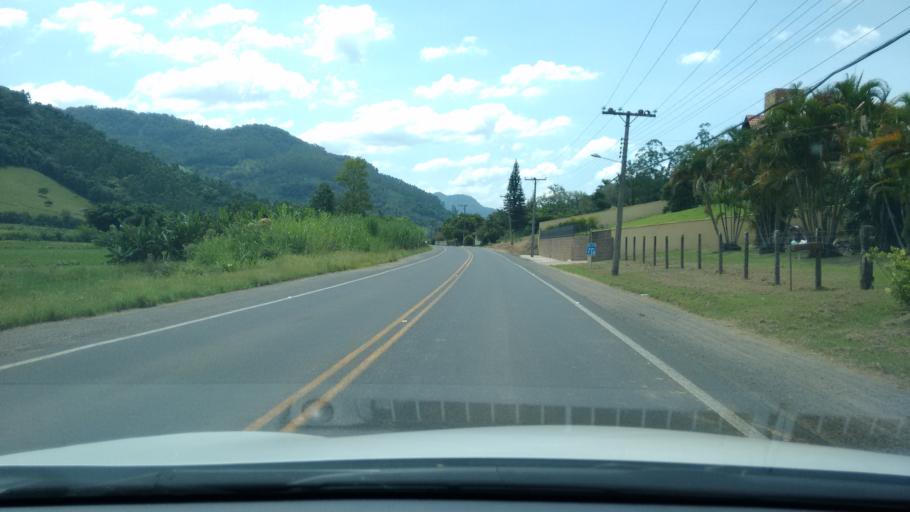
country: BR
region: Santa Catarina
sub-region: Rodeio
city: Gavea
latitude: -26.8751
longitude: -49.3410
